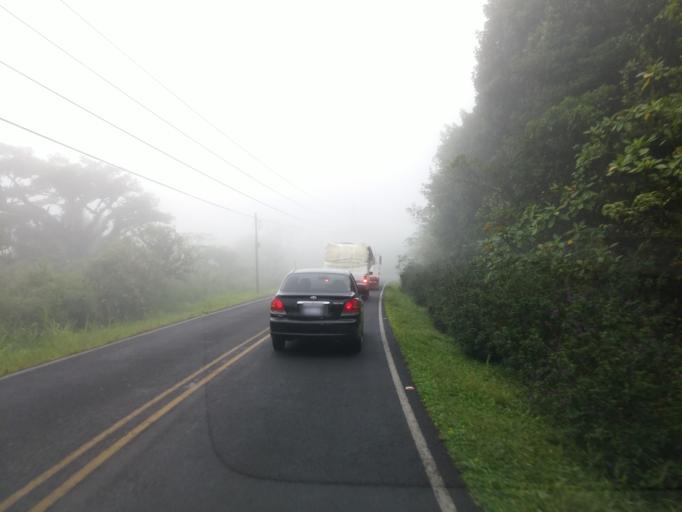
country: CR
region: Alajuela
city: San Ramon
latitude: 10.1821
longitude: -84.5071
